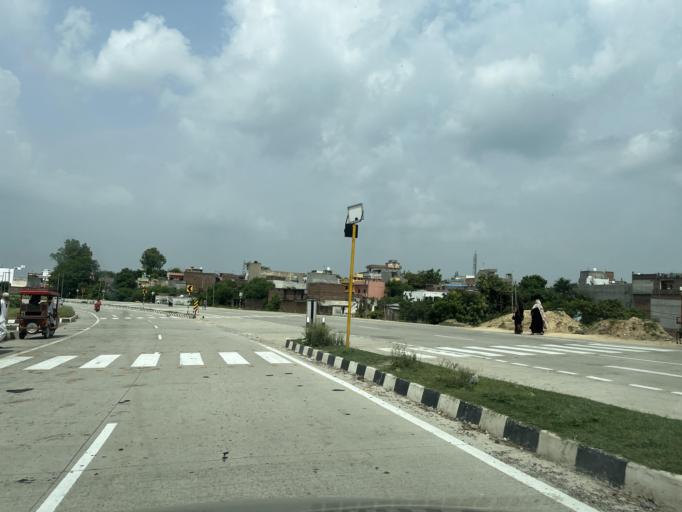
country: IN
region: Uttar Pradesh
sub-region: Bijnor
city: Sherkot
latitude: 29.3271
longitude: 78.5686
